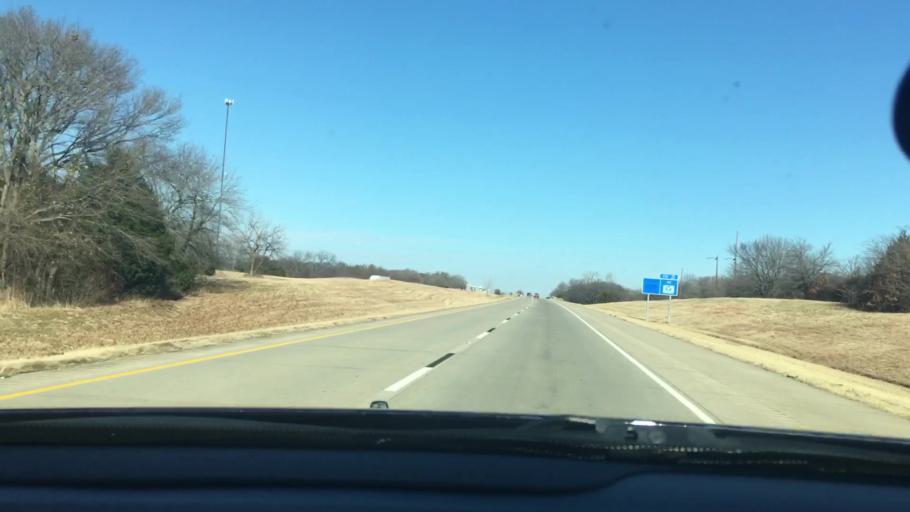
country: US
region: Oklahoma
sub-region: Love County
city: Marietta
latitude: 34.0094
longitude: -97.1425
